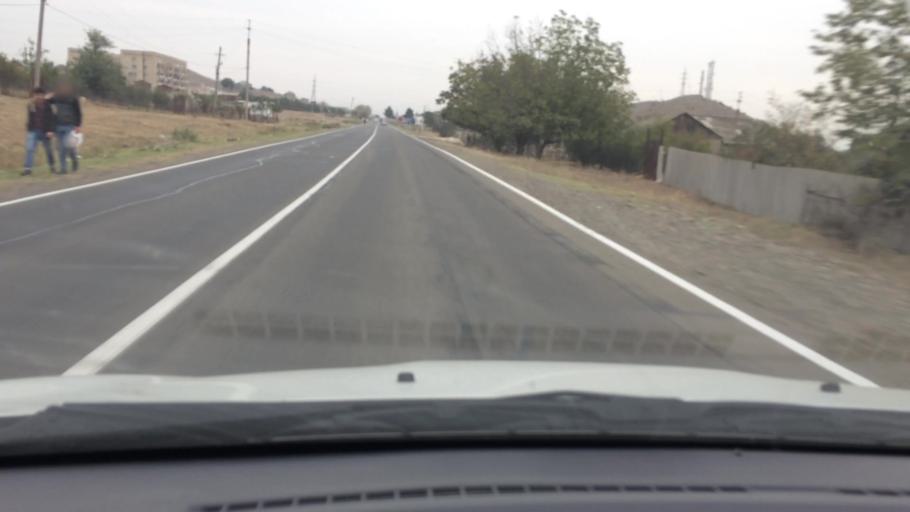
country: GE
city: Naghvarevi
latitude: 41.3583
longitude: 44.8320
